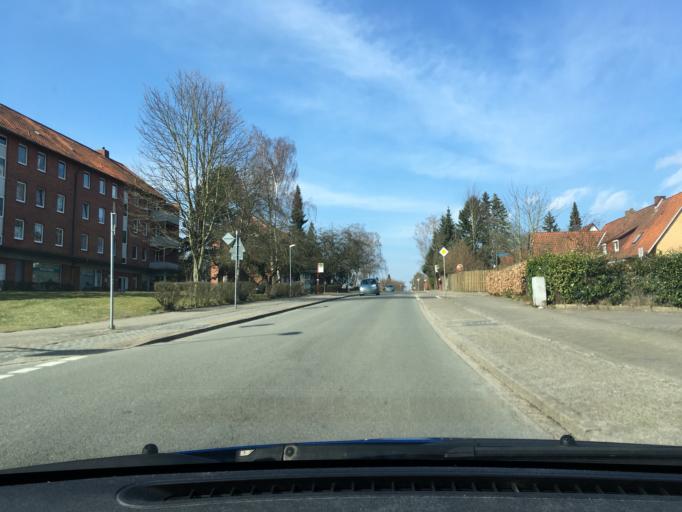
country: DE
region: Lower Saxony
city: Lueneburg
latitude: 53.2557
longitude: 10.3926
